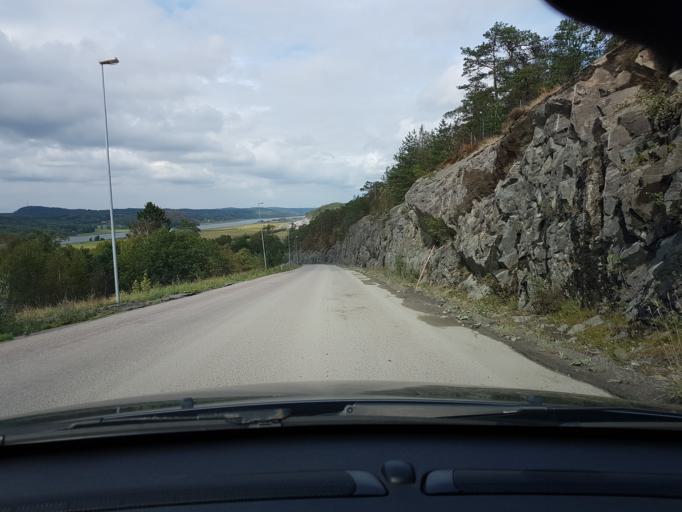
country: SE
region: Vaestra Goetaland
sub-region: Ale Kommun
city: Surte
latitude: 57.8674
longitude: 12.0341
